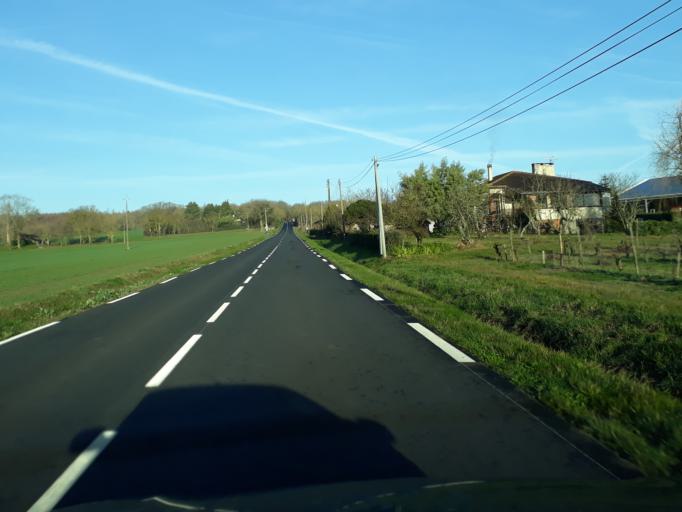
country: FR
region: Midi-Pyrenees
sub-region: Departement du Gers
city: Pujaudran
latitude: 43.5521
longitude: 1.1436
